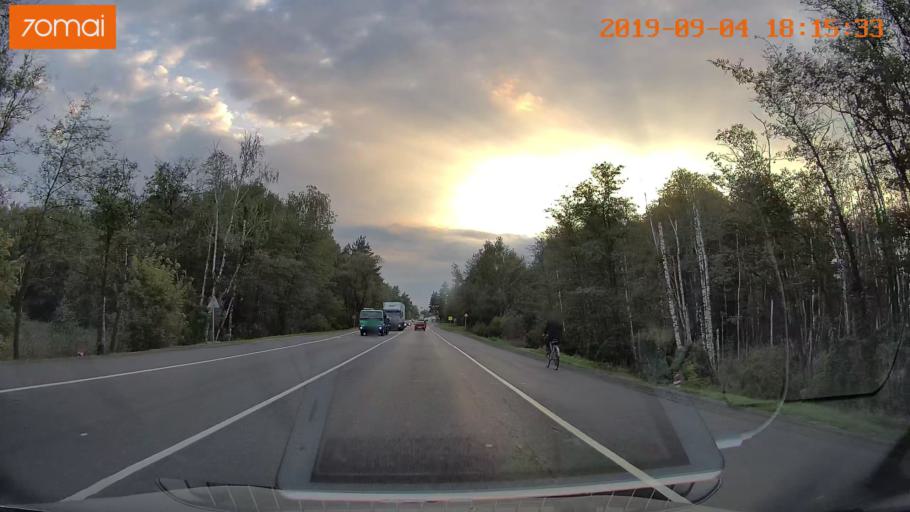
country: RU
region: Moskovskaya
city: Lopatinskiy
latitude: 55.3464
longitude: 38.7008
